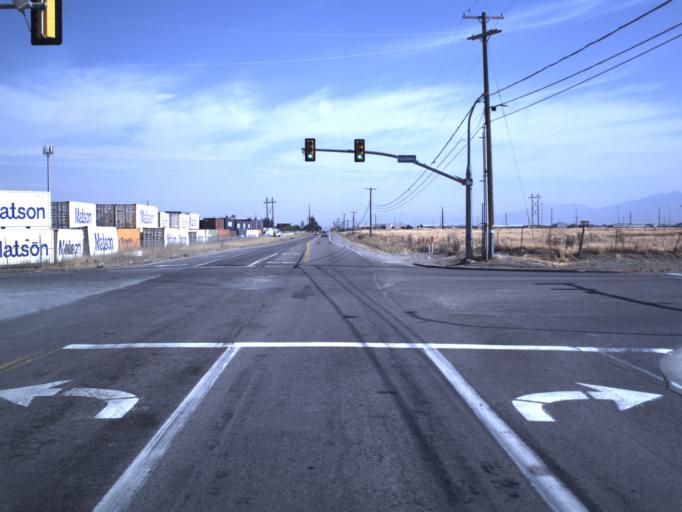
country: US
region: Utah
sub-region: Salt Lake County
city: West Valley City
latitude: 40.7399
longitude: -112.0249
